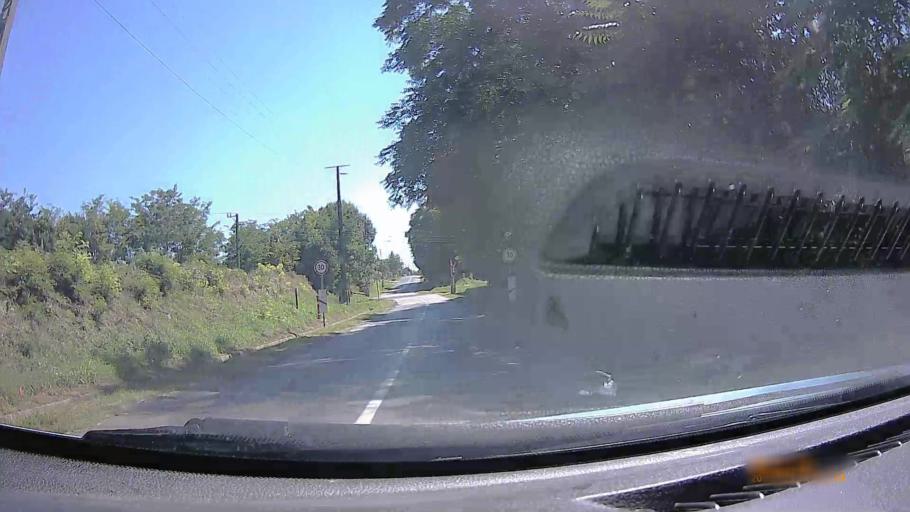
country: HU
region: Fejer
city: Cece
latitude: 46.7863
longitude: 18.5902
